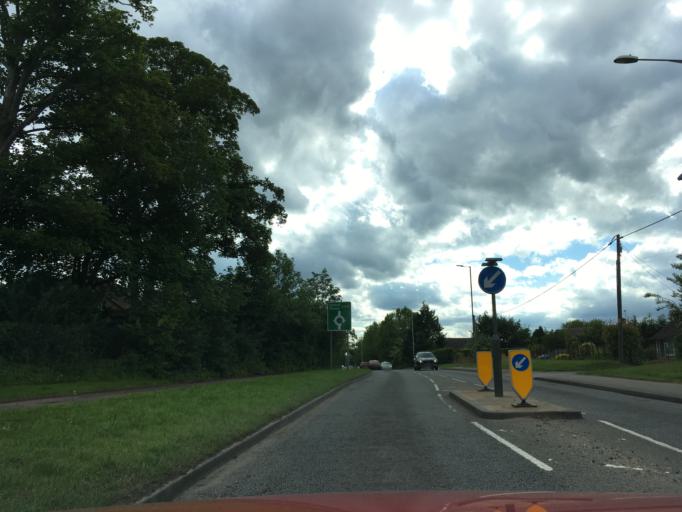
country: GB
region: England
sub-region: Buckinghamshire
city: Stone
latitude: 51.8035
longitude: -0.8684
